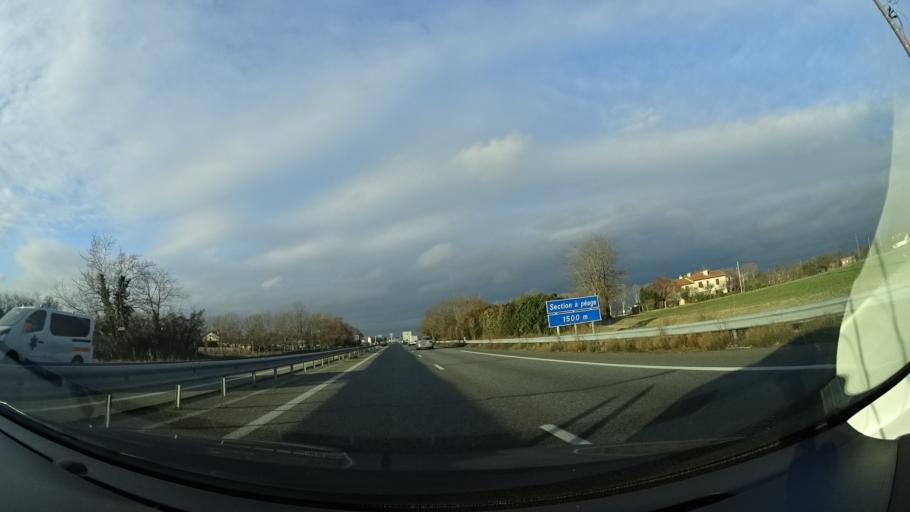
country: FR
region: Midi-Pyrenees
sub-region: Departement de l'Ariege
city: La Tour-du-Crieu
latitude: 43.1143
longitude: 1.6308
